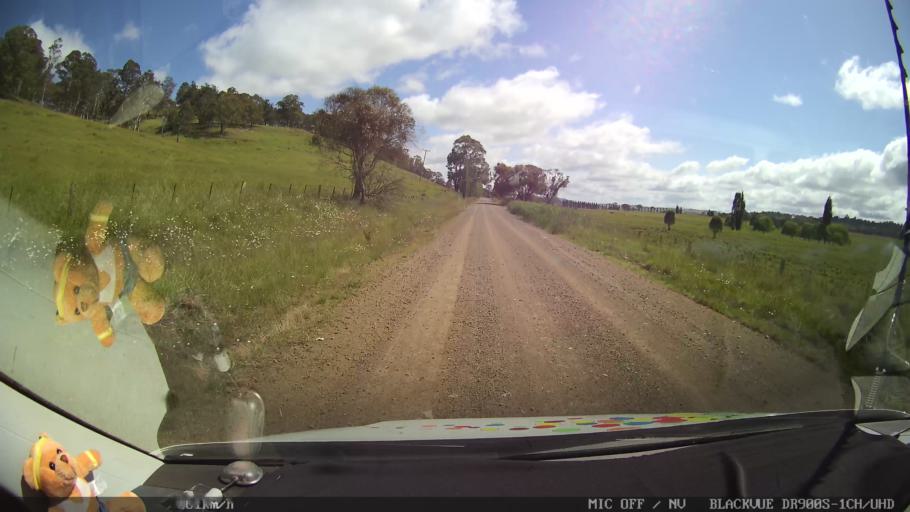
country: AU
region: New South Wales
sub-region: Glen Innes Severn
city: Glen Innes
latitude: -29.9565
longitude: 151.7030
